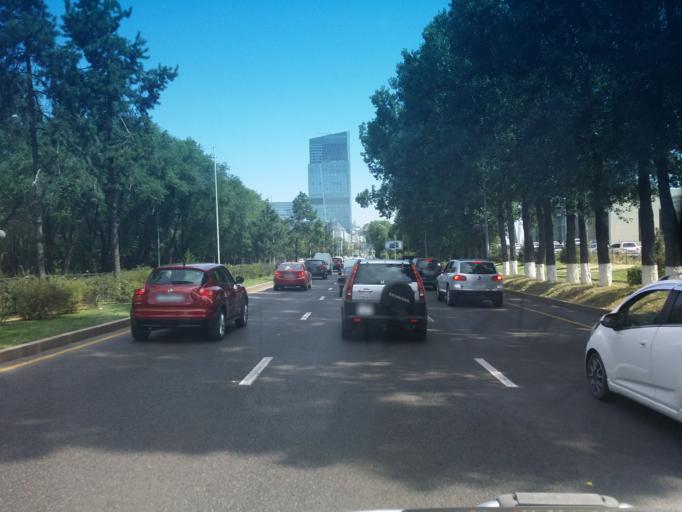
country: KZ
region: Almaty Qalasy
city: Almaty
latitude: 43.2136
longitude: 76.9223
